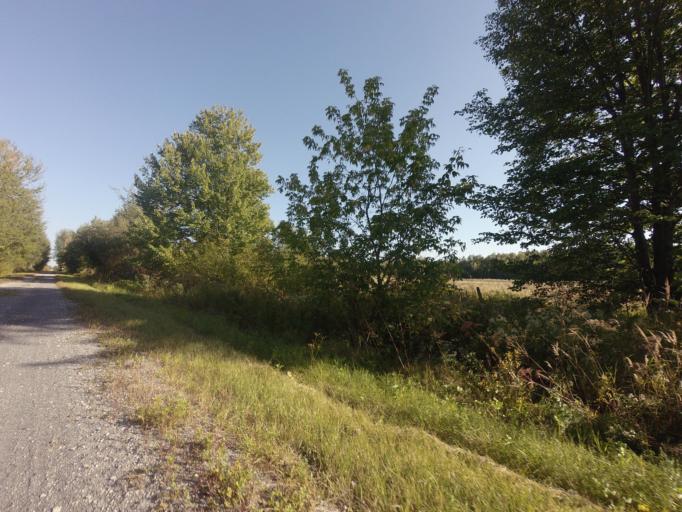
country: CA
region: Ontario
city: Hawkesbury
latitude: 45.5354
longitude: -74.5963
